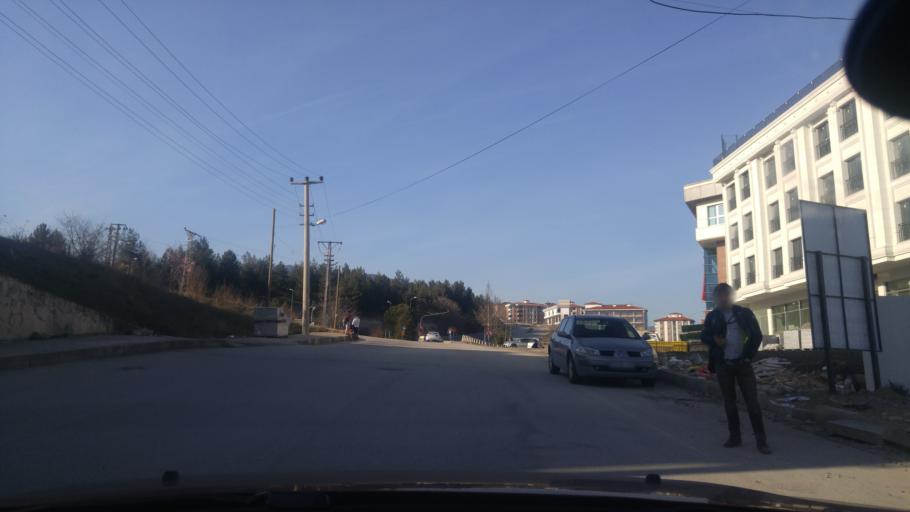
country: TR
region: Karabuk
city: Safranbolu
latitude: 41.2274
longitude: 32.6694
